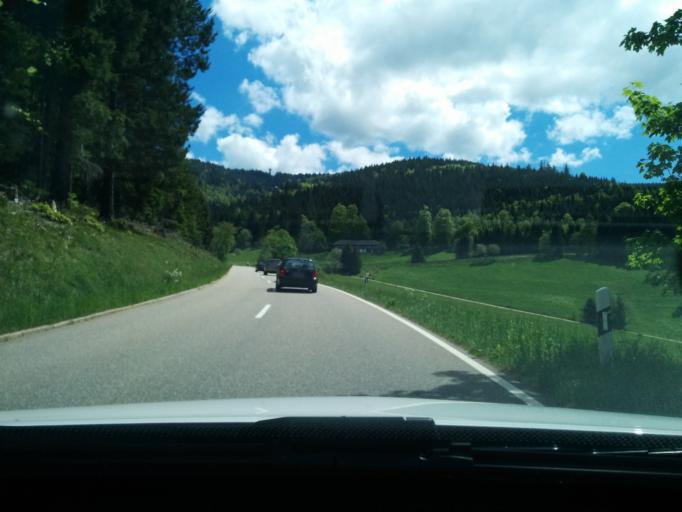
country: DE
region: Baden-Wuerttemberg
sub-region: Freiburg Region
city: Horben
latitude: 47.9153
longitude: 7.8777
